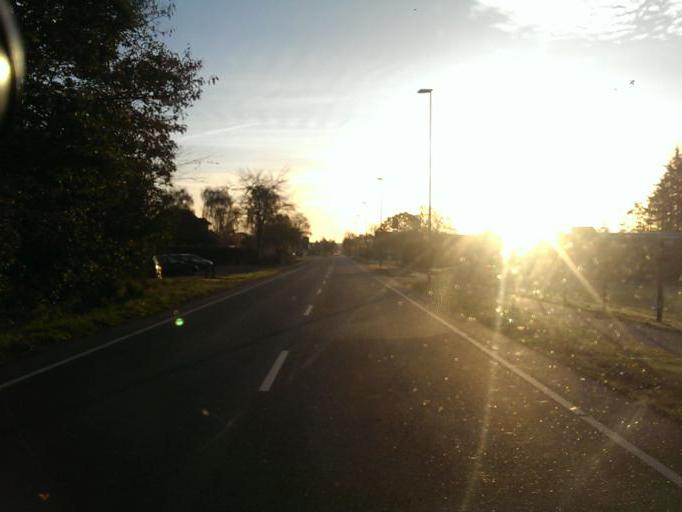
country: DK
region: South Denmark
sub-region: Esbjerg Kommune
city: Bramming
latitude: 55.4675
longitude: 8.6845
